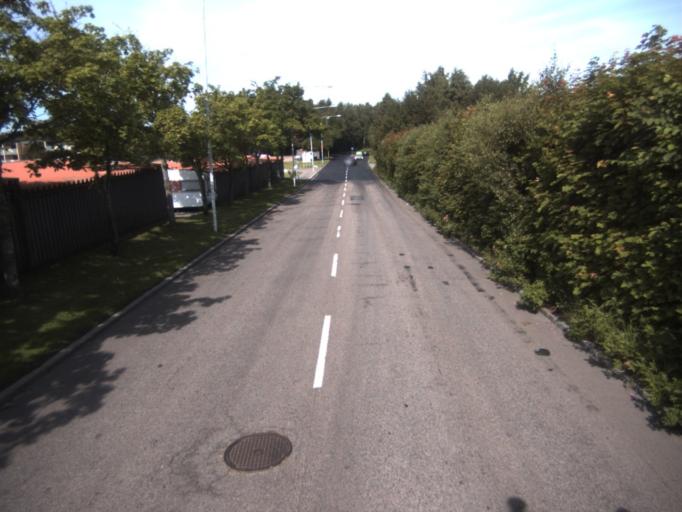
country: SE
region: Skane
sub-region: Helsingborg
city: Helsingborg
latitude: 56.0487
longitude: 12.7436
